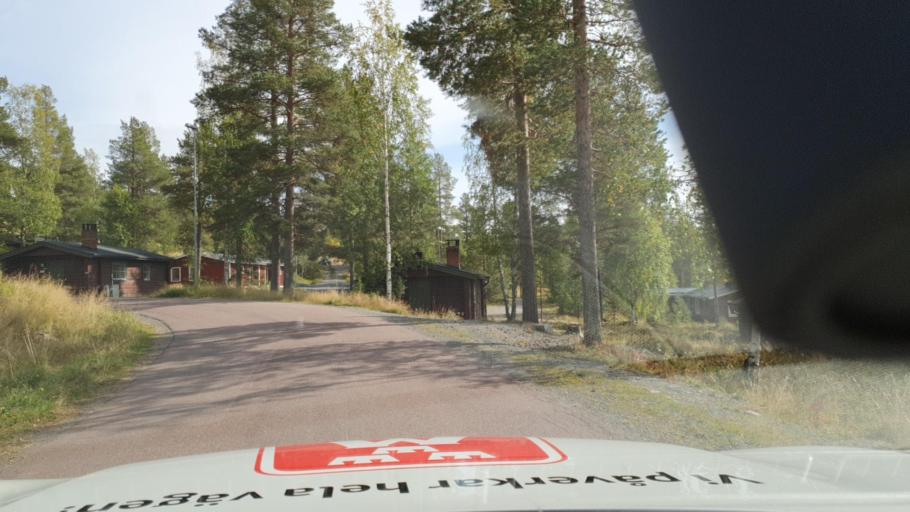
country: NO
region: Hedmark
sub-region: Trysil
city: Innbygda
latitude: 61.8870
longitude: 12.8343
